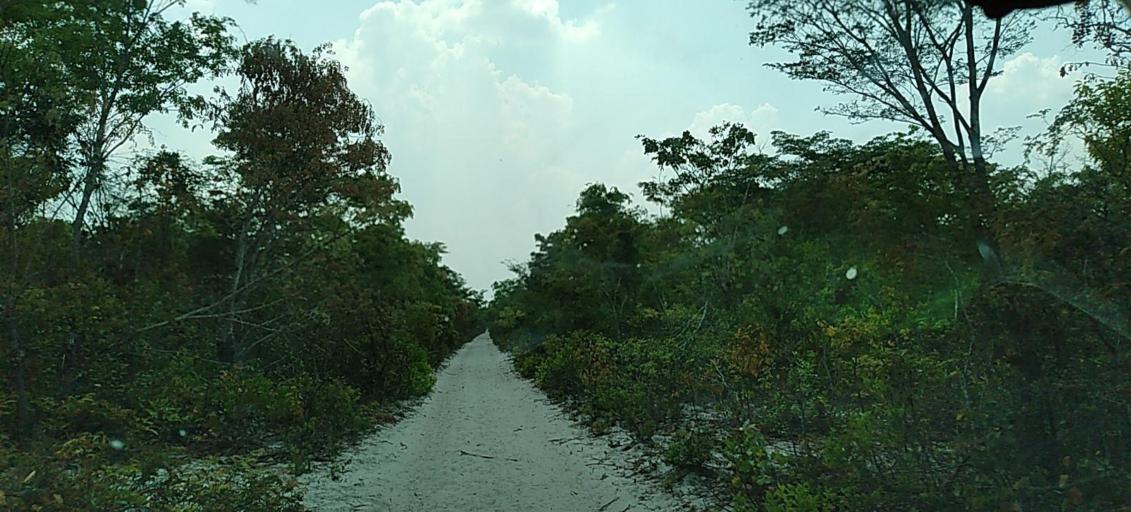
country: ZM
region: North-Western
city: Kabompo
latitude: -13.4003
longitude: 23.8110
